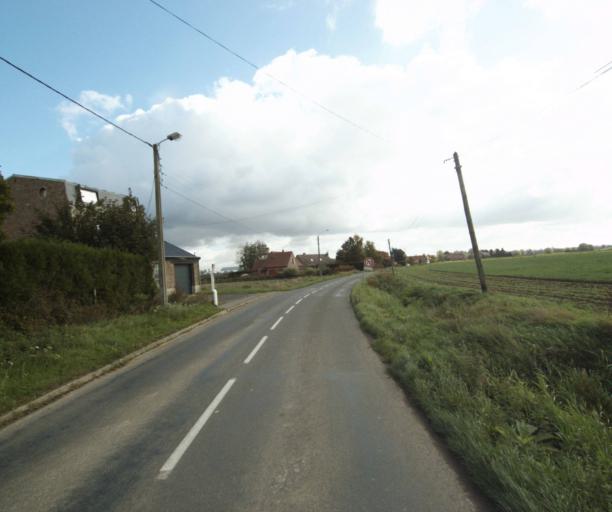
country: FR
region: Nord-Pas-de-Calais
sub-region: Departement du Nord
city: Perenchies
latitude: 50.6886
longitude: 2.9472
